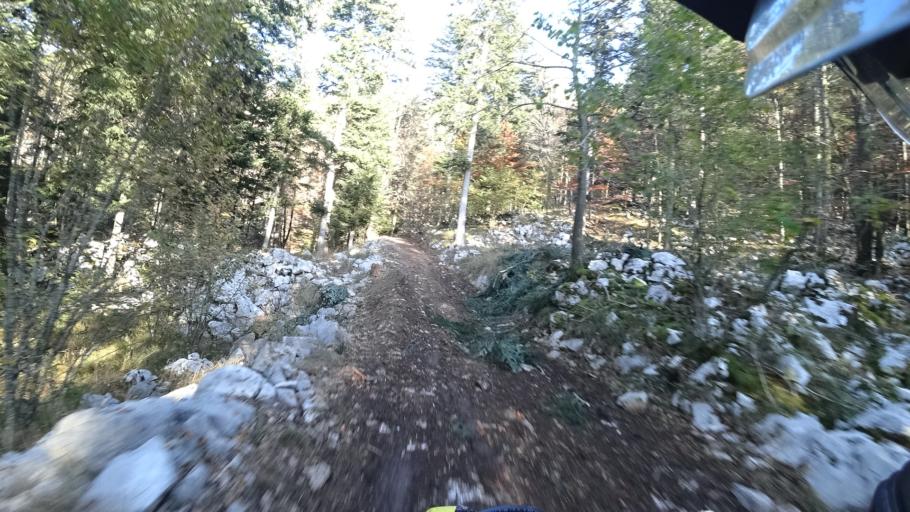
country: HR
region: Primorsko-Goranska
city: Klana
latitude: 45.4807
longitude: 14.4363
